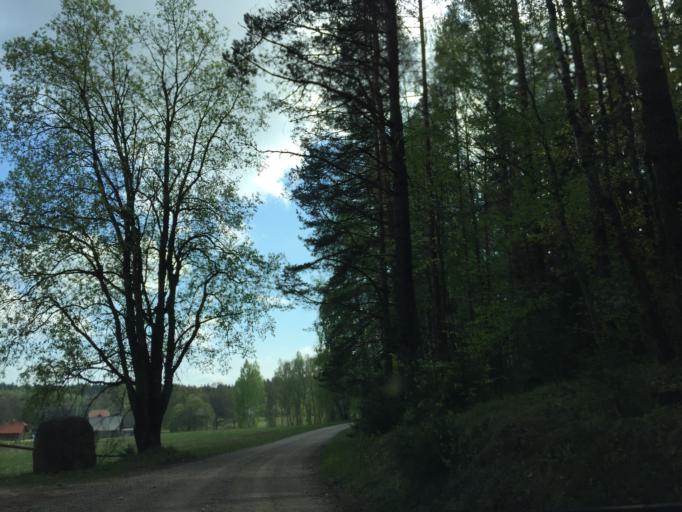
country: LV
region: Ligatne
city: Ligatne
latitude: 57.2911
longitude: 24.9390
